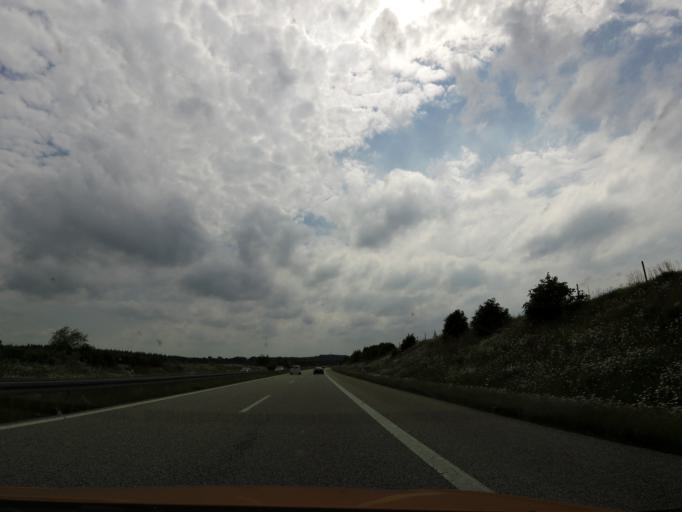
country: DE
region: Mecklenburg-Vorpommern
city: Leezen
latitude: 53.6347
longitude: 11.5176
